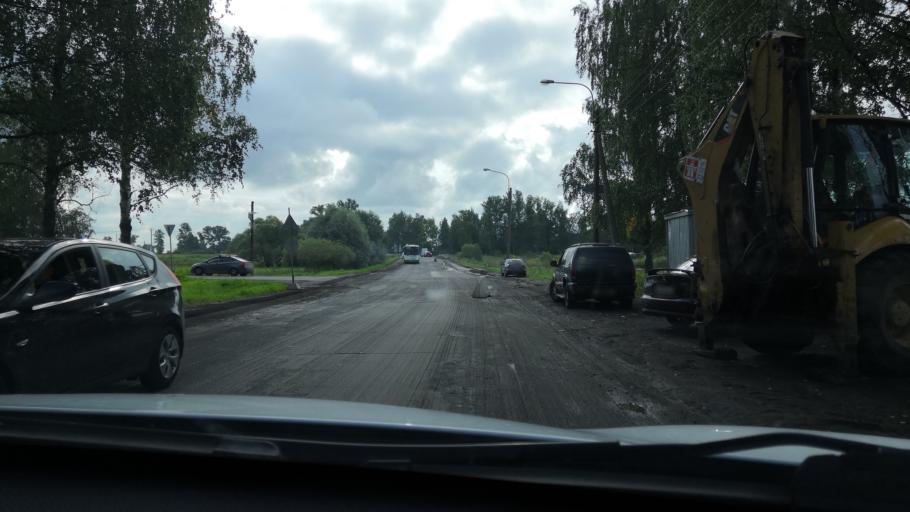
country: RU
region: St.-Petersburg
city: Tyarlevo
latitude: 59.7119
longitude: 30.4657
